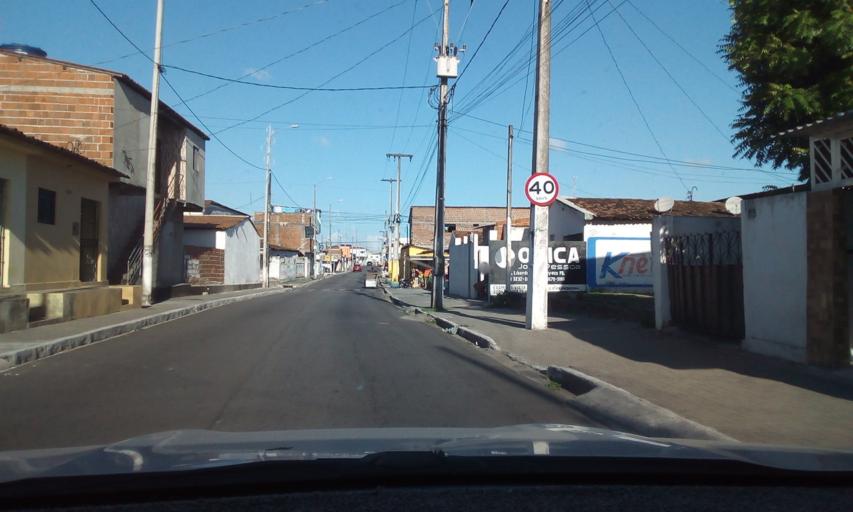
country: BR
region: Paraiba
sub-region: Bayeux
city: Bayeux
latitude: -7.1230
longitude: -34.9094
